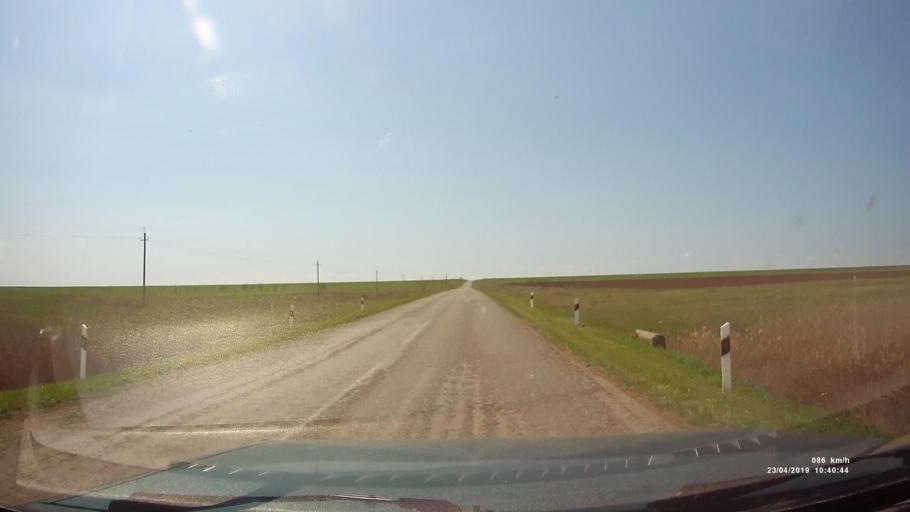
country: RU
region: Kalmykiya
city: Yashalta
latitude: 46.5026
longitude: 42.6384
